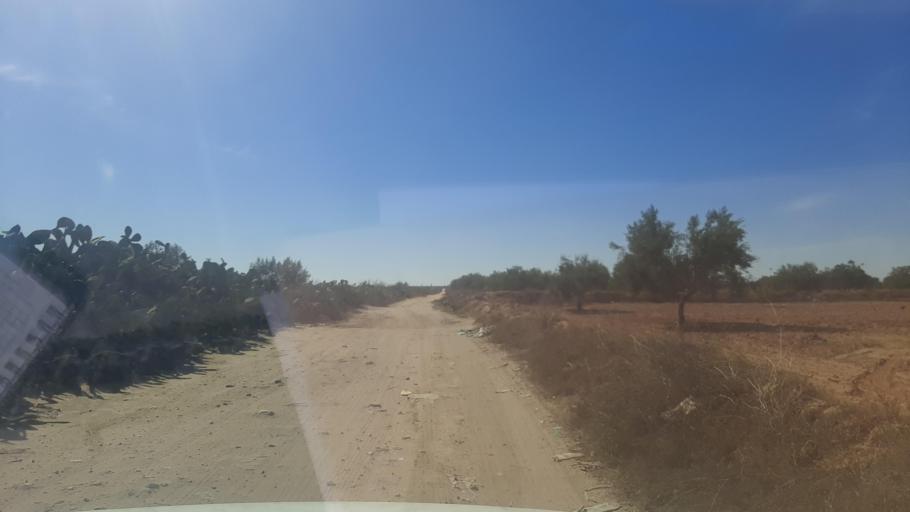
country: TN
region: Safaqis
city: Sfax
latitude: 34.8453
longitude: 10.5609
